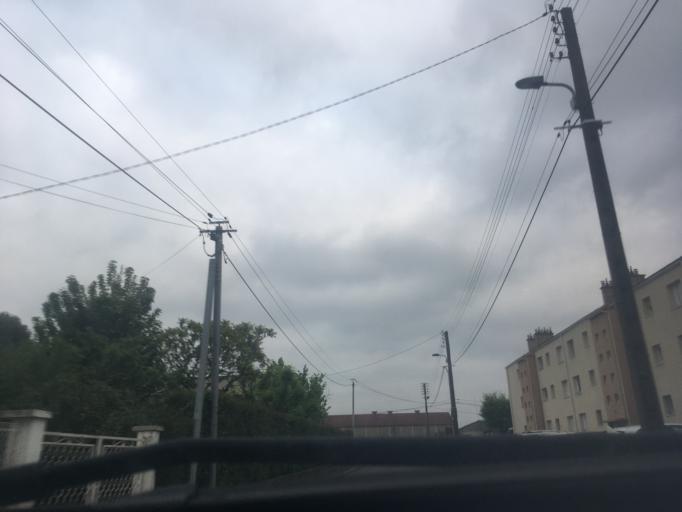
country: FR
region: Poitou-Charentes
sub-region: Departement de la Charente
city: Chateaubernard
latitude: 45.6828
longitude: -0.3353
